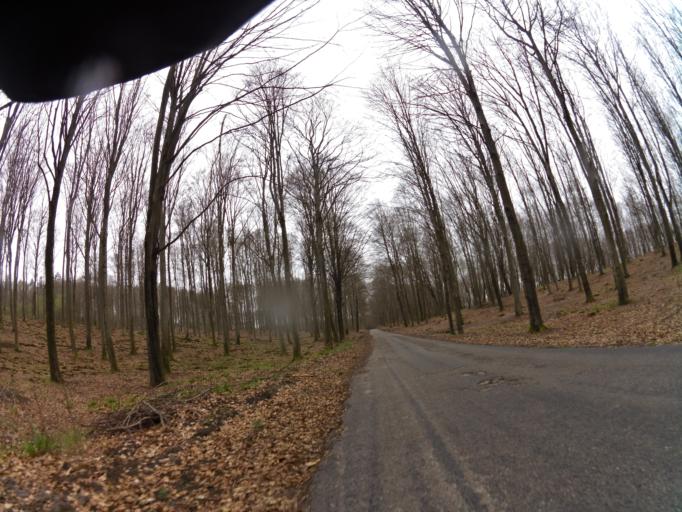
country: PL
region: West Pomeranian Voivodeship
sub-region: Powiat koszalinski
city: Bobolice
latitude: 53.9534
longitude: 16.6669
